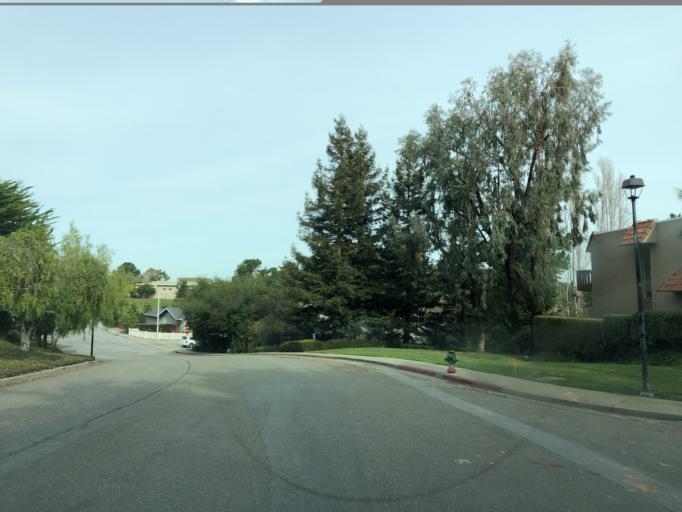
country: US
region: California
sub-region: San Mateo County
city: Highlands-Baywood Park
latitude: 37.5074
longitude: -122.3217
